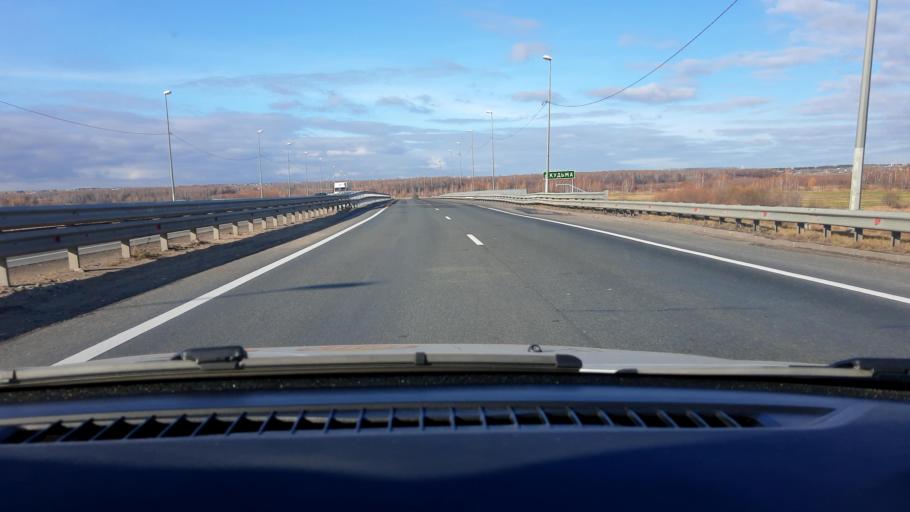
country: RU
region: Nizjnij Novgorod
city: Burevestnik
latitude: 56.1216
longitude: 43.8094
